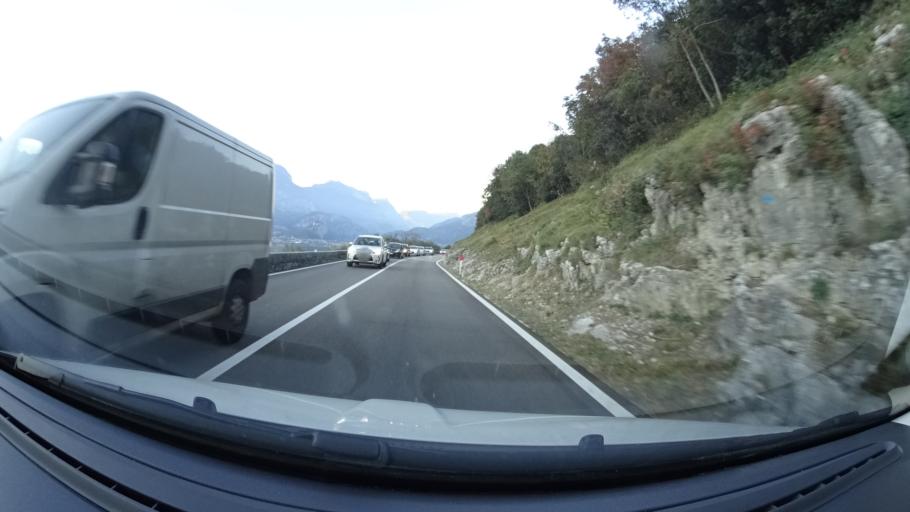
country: IT
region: Trentino-Alto Adige
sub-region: Provincia di Trento
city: Nago-Torbole
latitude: 45.8882
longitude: 10.8865
